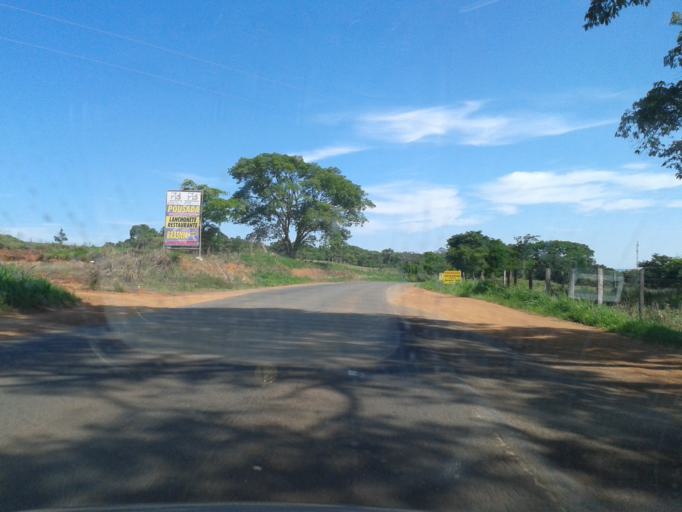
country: BR
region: Goias
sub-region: Piracanjuba
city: Piracanjuba
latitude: -17.2280
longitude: -48.7135
